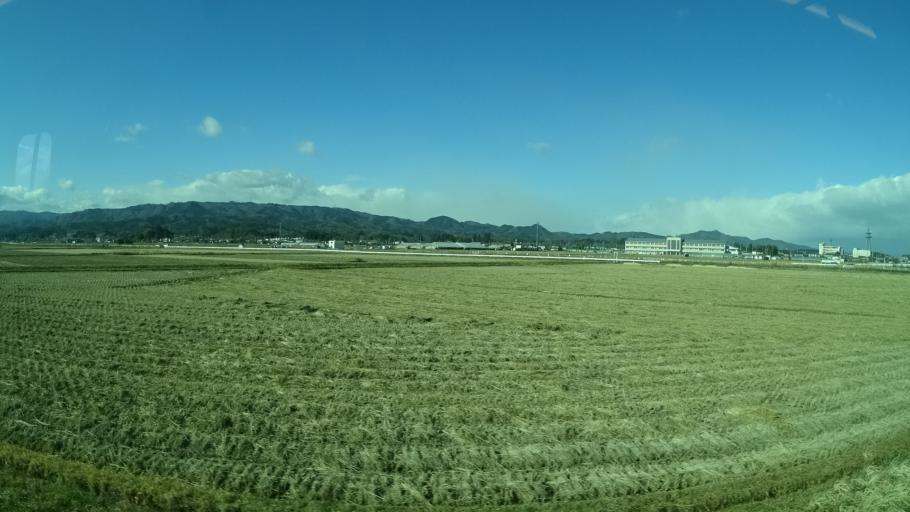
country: JP
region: Miyagi
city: Marumori
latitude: 37.7882
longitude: 140.9239
